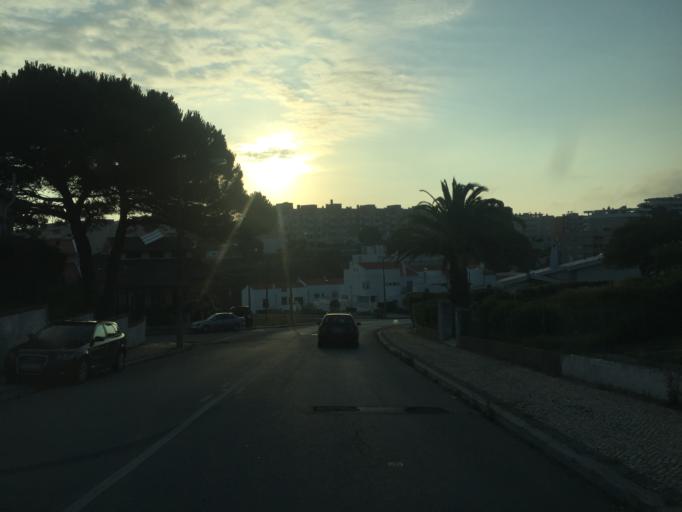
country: PT
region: Coimbra
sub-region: Figueira da Foz
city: Figueira da Foz
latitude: 40.1577
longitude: -8.8637
